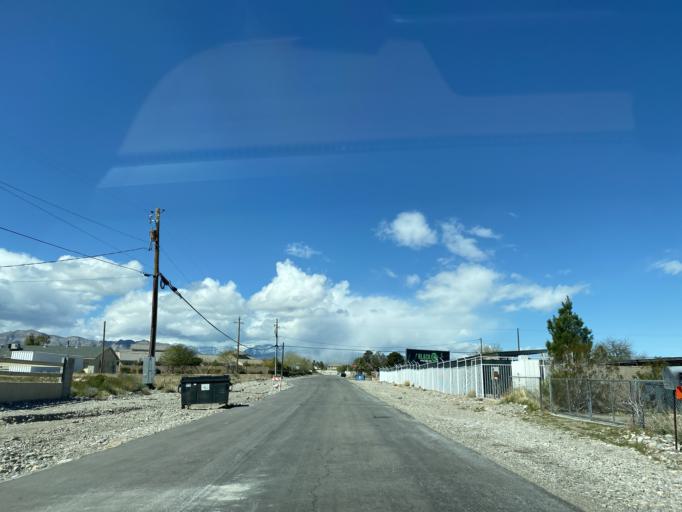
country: US
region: Nevada
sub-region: Clark County
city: North Las Vegas
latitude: 36.3195
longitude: -115.2816
